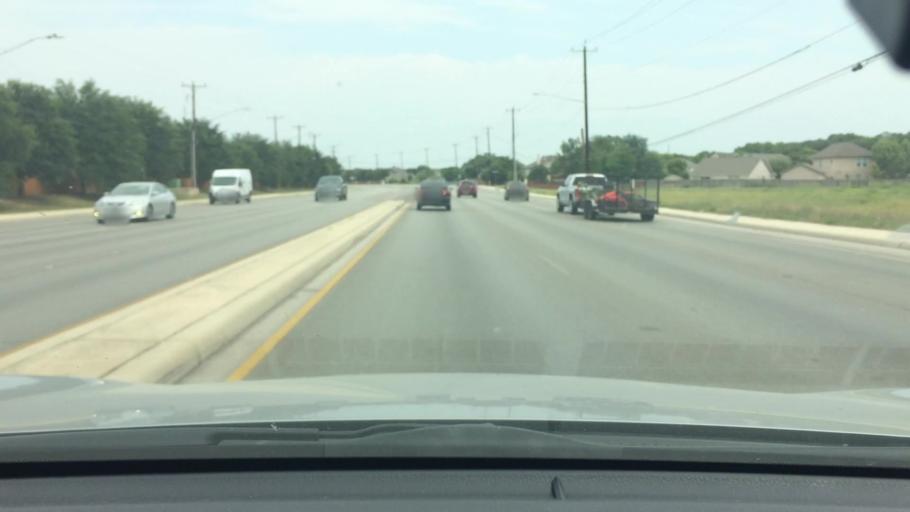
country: US
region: Texas
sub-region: Bexar County
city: Leon Valley
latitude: 29.4775
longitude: -98.6625
